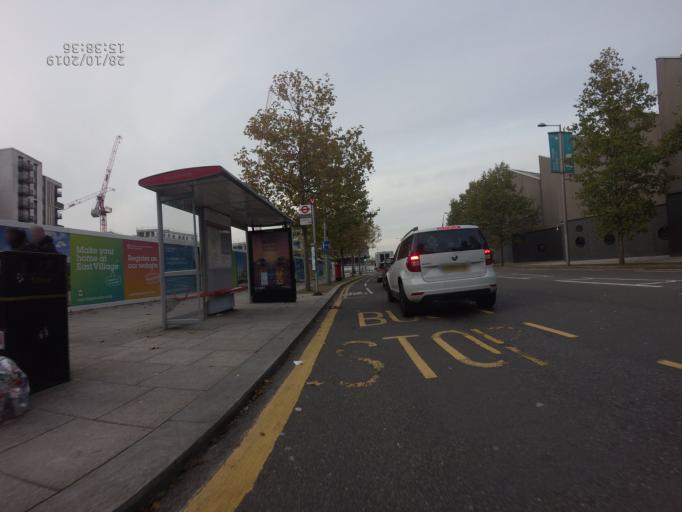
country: GB
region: England
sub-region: Greater London
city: Poplar
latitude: 51.5490
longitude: -0.0084
